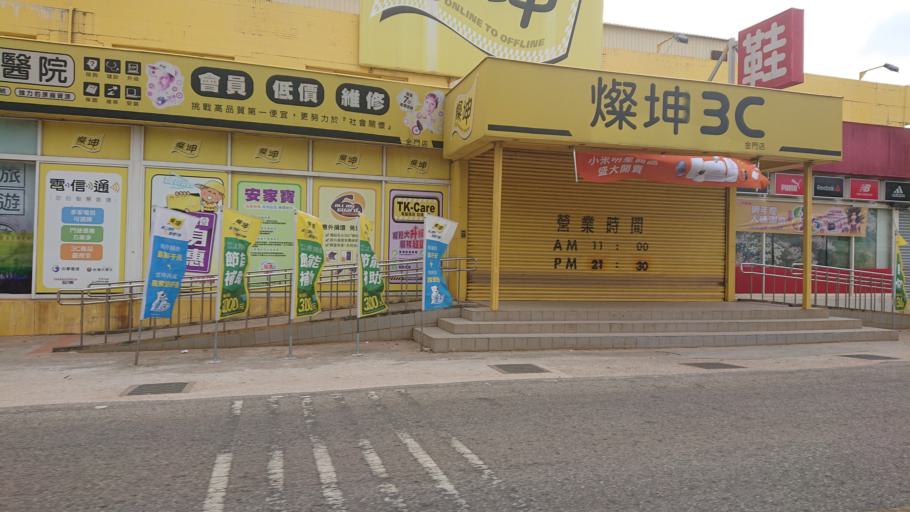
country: TW
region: Fukien
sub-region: Kinmen
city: Jincheng
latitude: 24.4289
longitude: 118.3214
